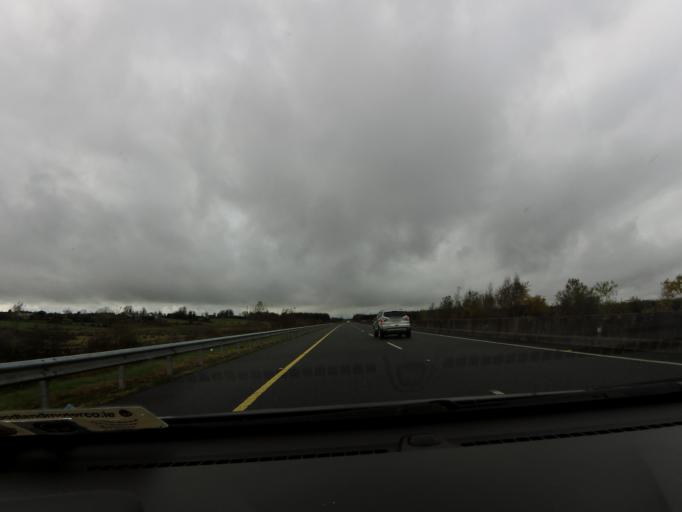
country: IE
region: Connaught
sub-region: County Galway
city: Loughrea
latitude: 53.2835
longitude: -8.4929
